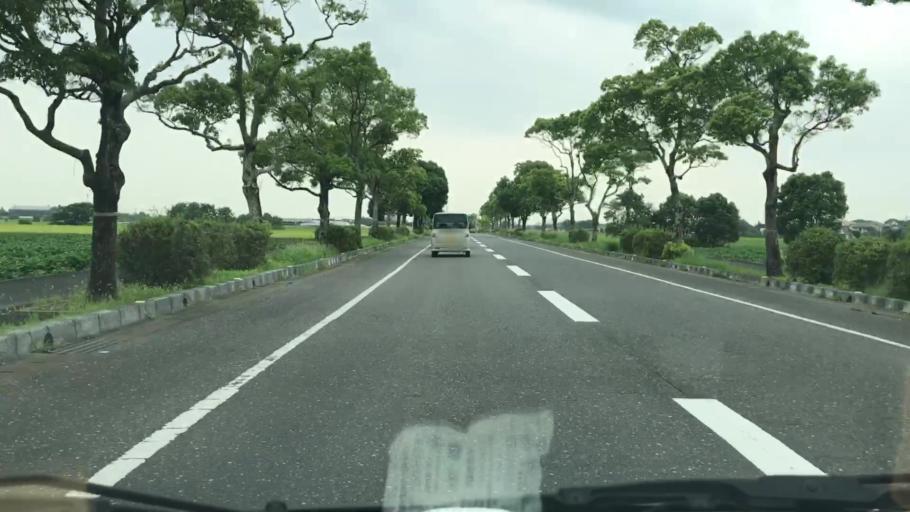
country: JP
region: Saga Prefecture
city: Saga-shi
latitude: 33.2312
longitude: 130.3060
